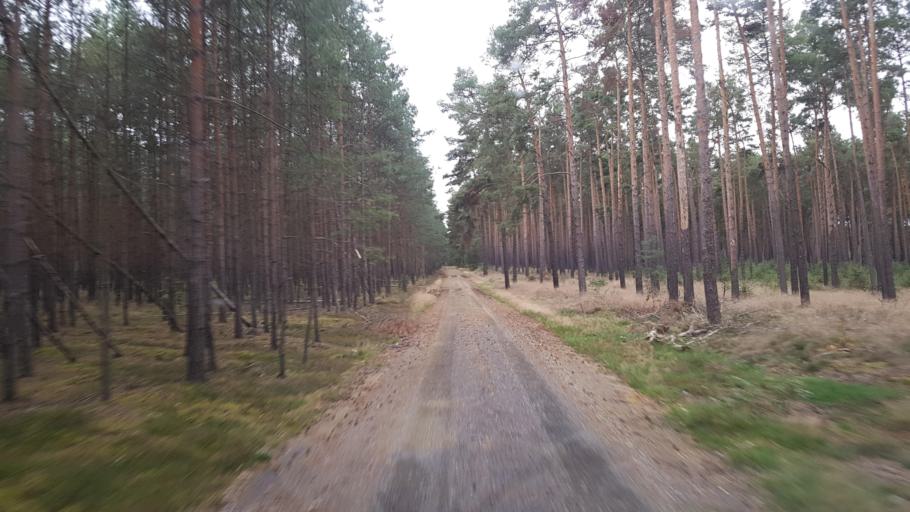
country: DE
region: Brandenburg
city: Sonnewalde
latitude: 51.7329
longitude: 13.6604
